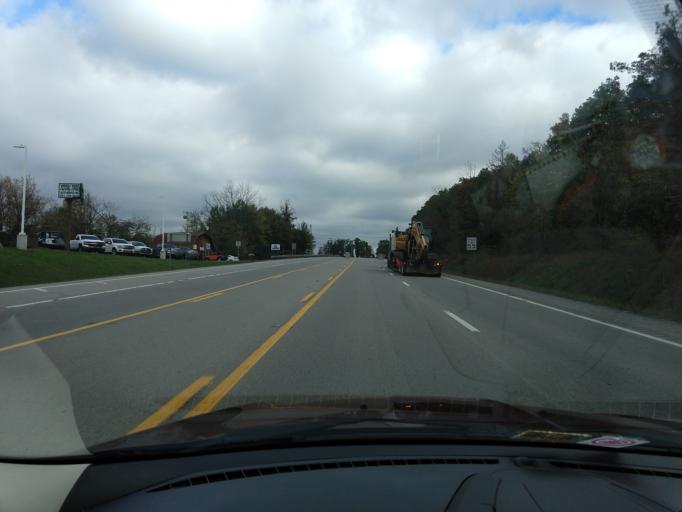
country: US
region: West Virginia
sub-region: Randolph County
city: Elkins
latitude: 38.8504
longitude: -79.8676
